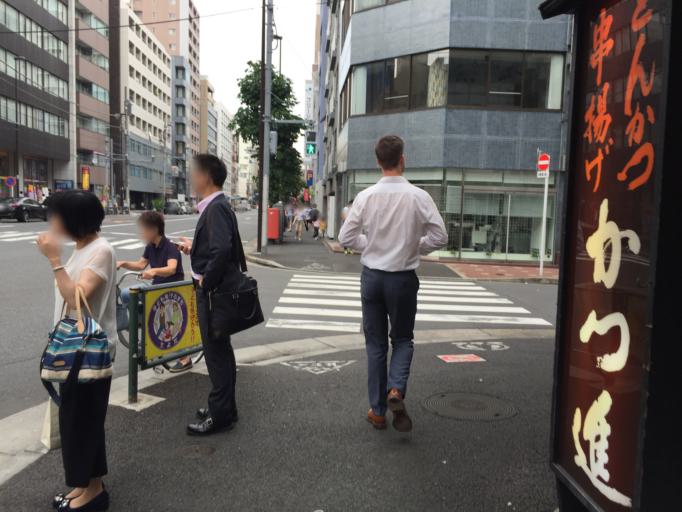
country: JP
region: Tokyo
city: Tokyo
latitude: 35.7045
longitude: 139.7699
